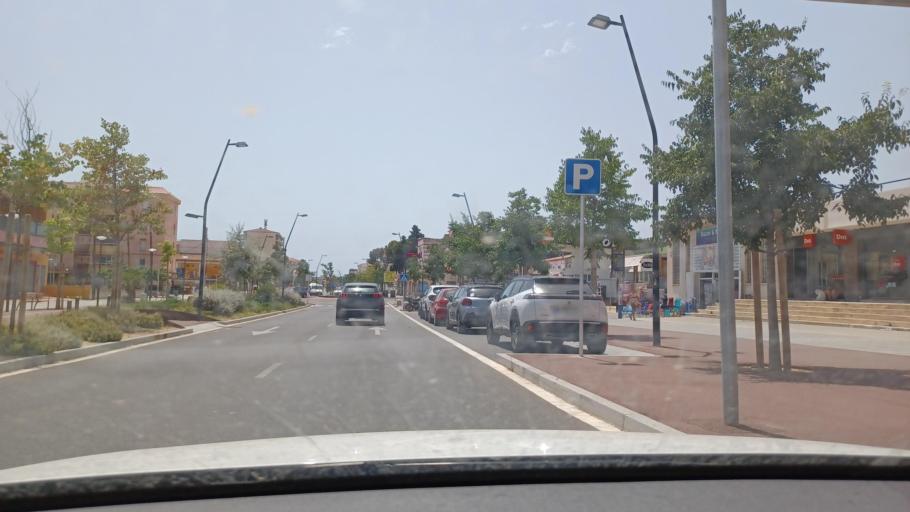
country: ES
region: Catalonia
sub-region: Provincia de Tarragona
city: Colldejou
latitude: 41.0074
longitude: 0.9367
